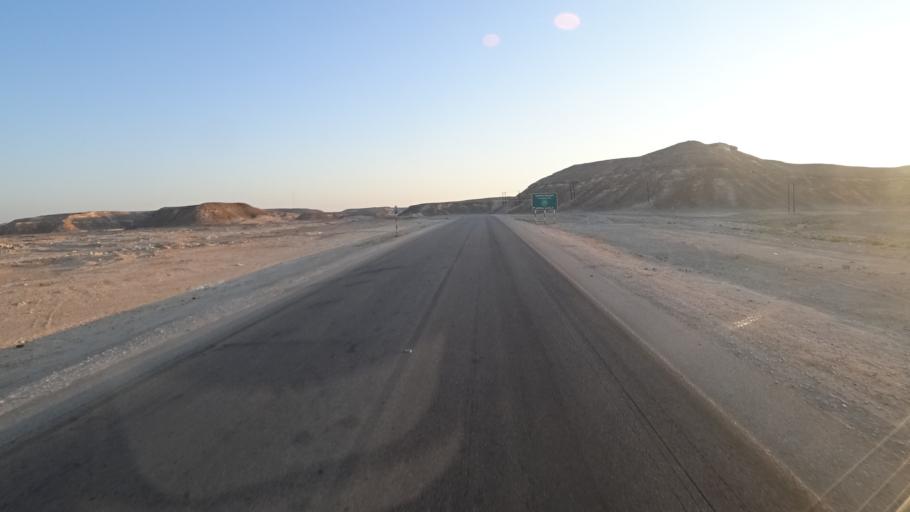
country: OM
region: Zufar
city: Salalah
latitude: 17.5014
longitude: 53.3627
